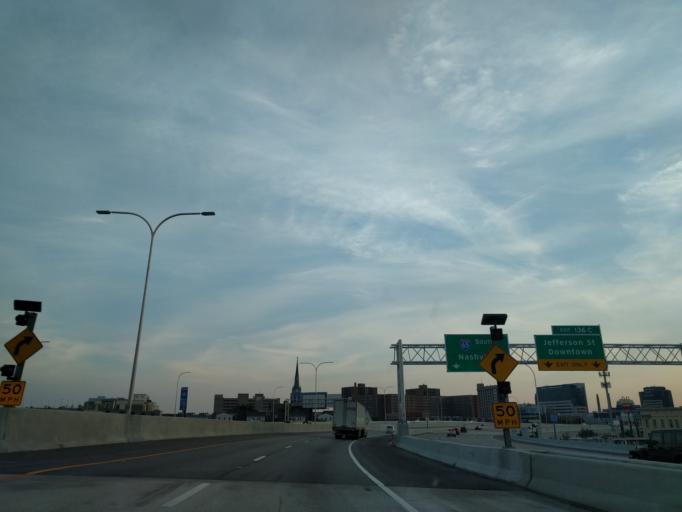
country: US
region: Kentucky
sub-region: Jefferson County
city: Louisville
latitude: 38.2551
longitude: -85.7424
